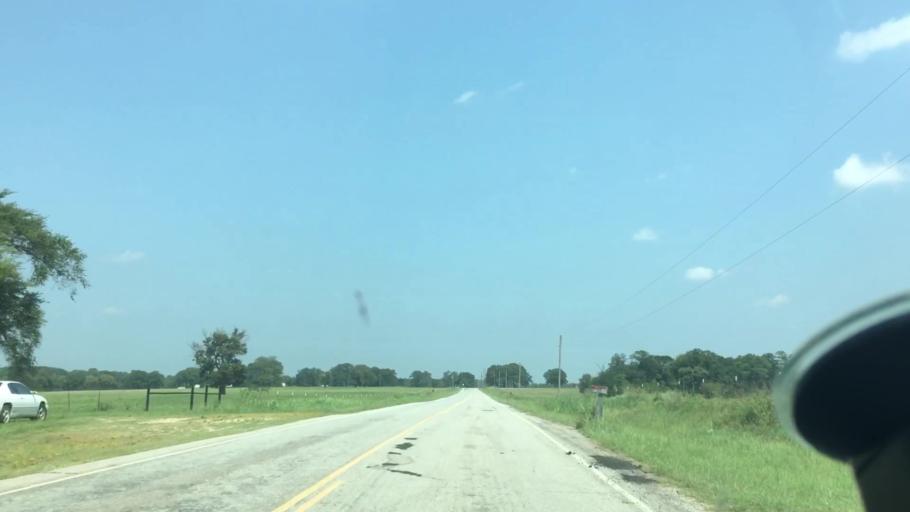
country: US
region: Oklahoma
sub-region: Atoka County
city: Atoka
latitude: 34.2727
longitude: -95.9361
